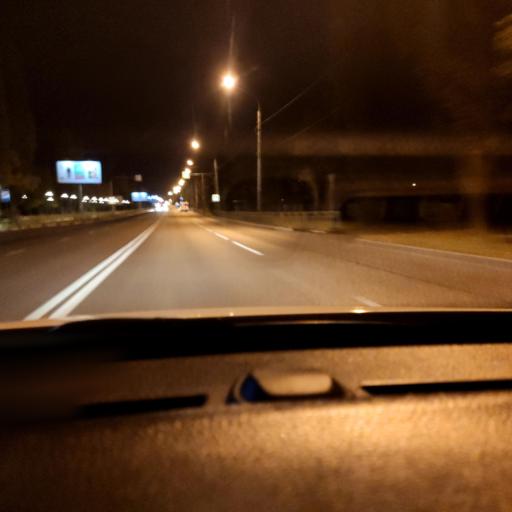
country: RU
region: Voronezj
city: Voronezh
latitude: 51.6682
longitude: 39.2623
